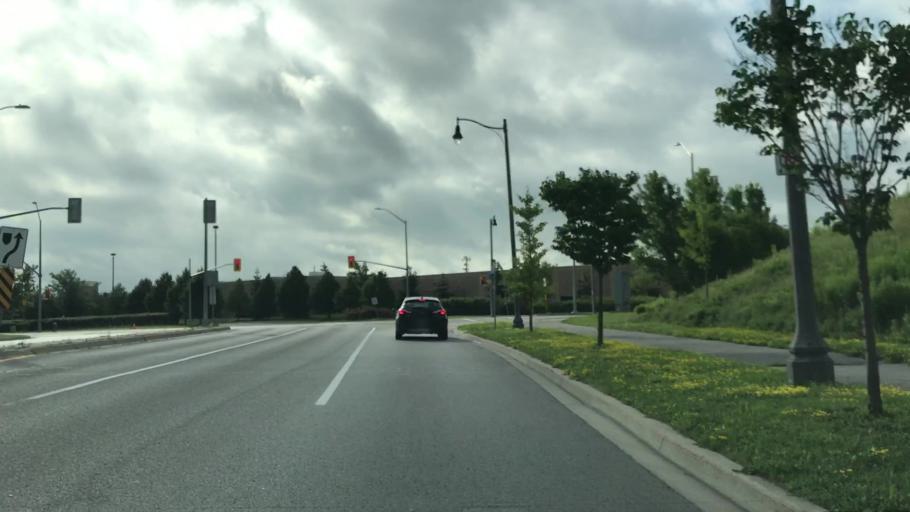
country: CA
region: Ontario
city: Newmarket
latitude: 44.0166
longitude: -79.4153
